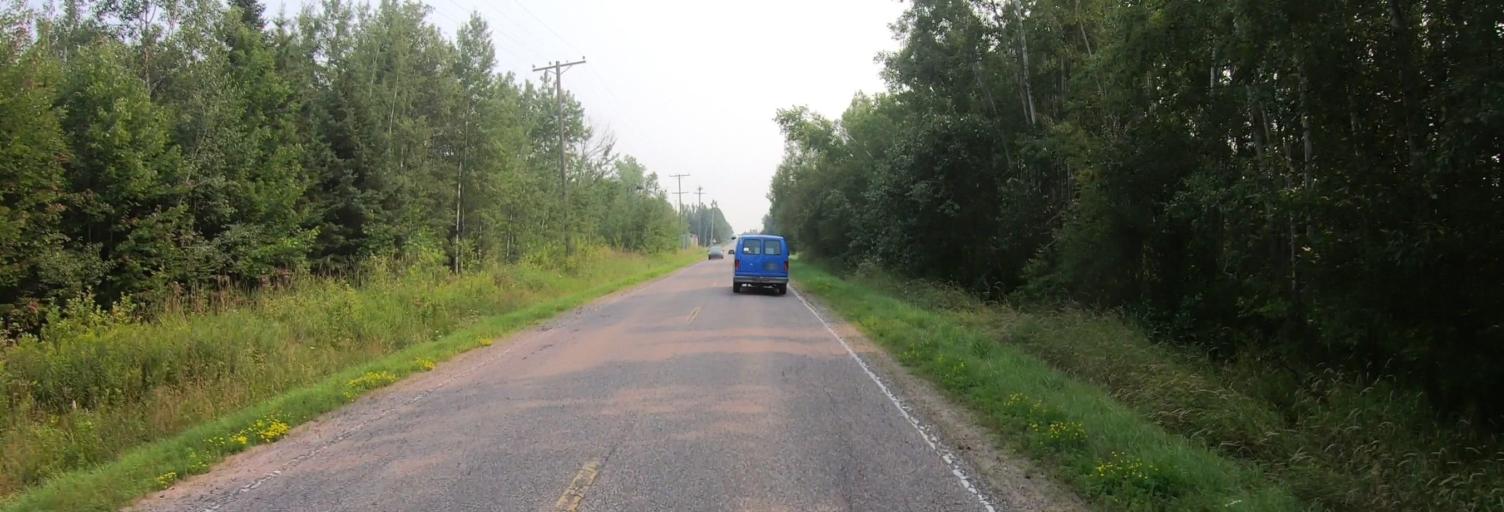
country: US
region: Michigan
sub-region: Chippewa County
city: Sault Ste. Marie
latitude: 46.4647
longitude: -84.3013
